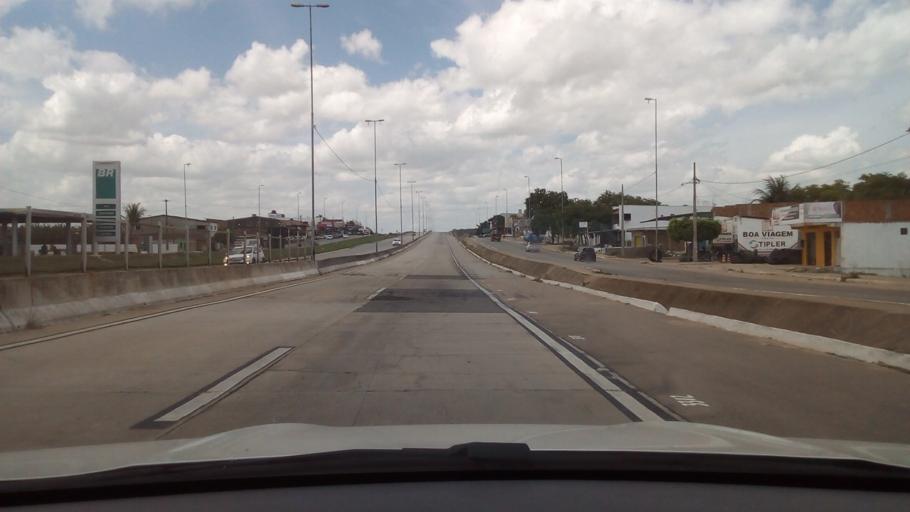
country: BR
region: Paraiba
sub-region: Mamanguape
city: Mamanguape
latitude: -6.8439
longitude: -35.1358
